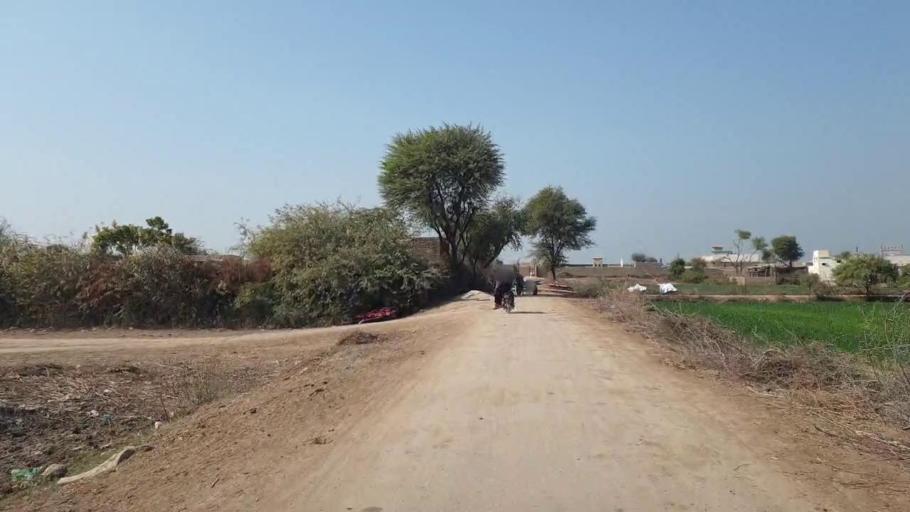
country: PK
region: Sindh
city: Hala
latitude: 25.9089
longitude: 68.4455
